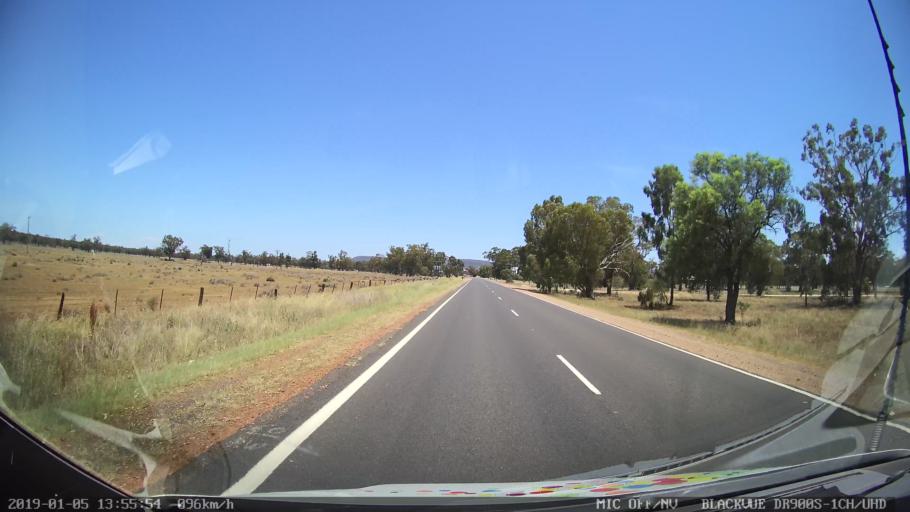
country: AU
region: New South Wales
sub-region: Gunnedah
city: Gunnedah
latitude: -31.1094
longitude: 150.2698
